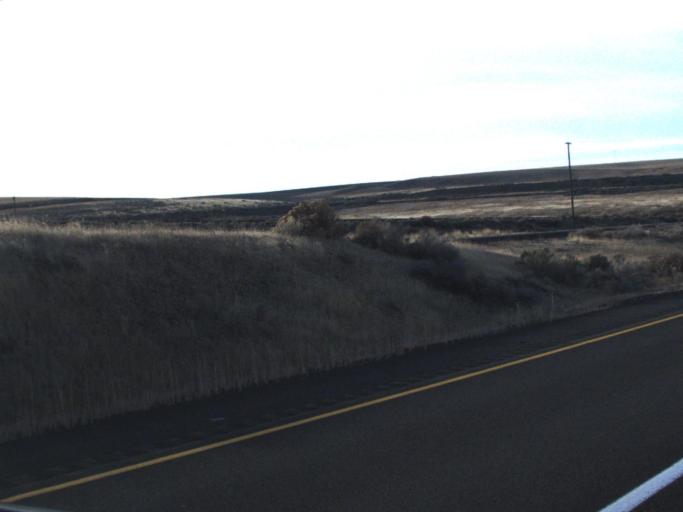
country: US
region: Washington
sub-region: Adams County
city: Ritzville
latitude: 46.9694
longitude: -118.5690
